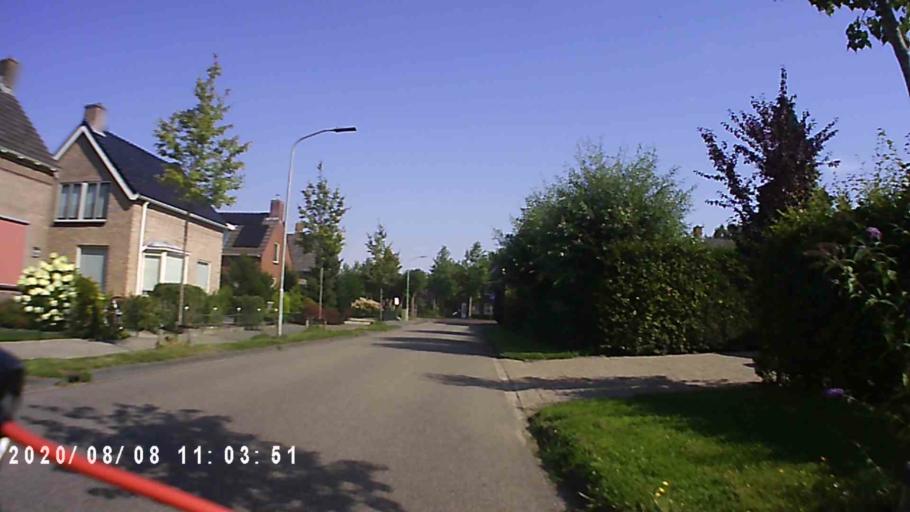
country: NL
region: Groningen
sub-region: Gemeente Leek
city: Leek
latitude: 53.1601
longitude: 6.3944
